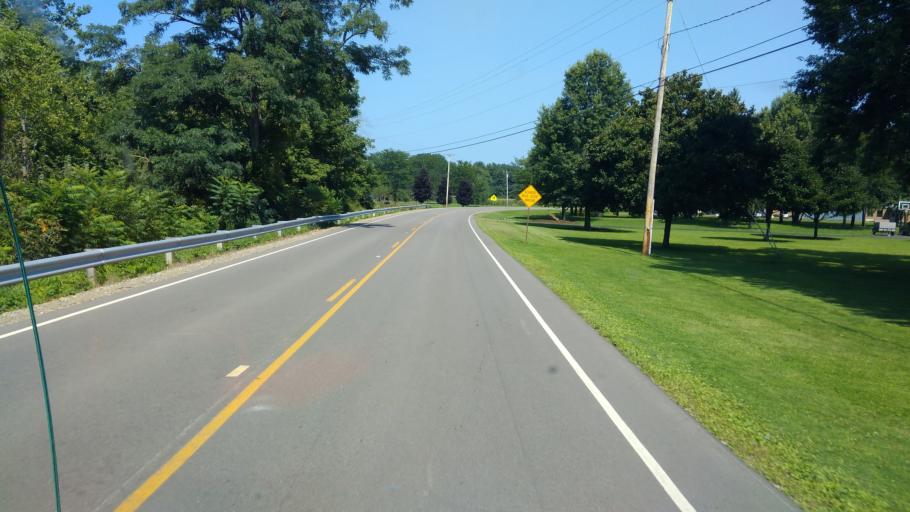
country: US
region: New York
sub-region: Allegany County
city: Belmont
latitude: 42.2372
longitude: -78.0399
